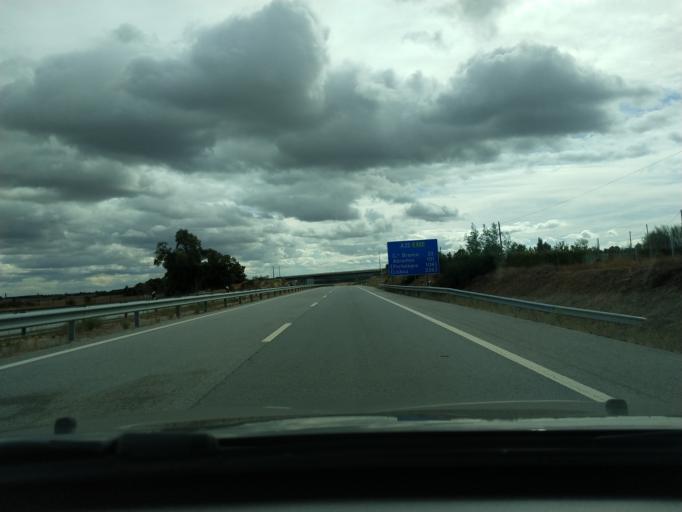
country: PT
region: Guarda
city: Alcains
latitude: 40.0197
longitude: -7.4661
